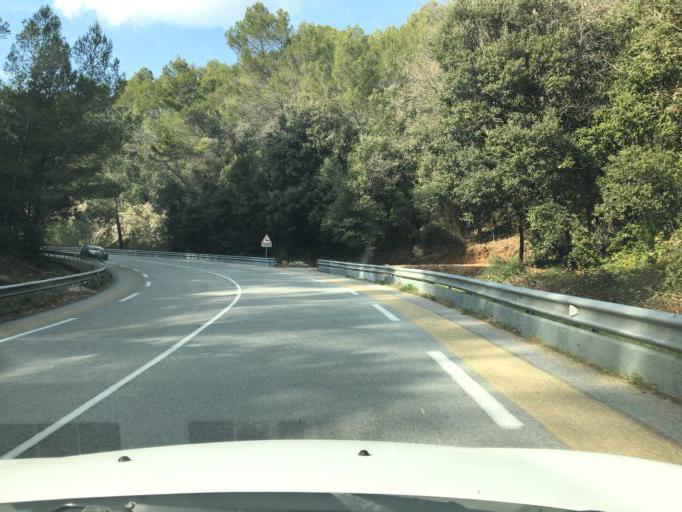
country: FR
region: Provence-Alpes-Cote d'Azur
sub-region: Departement du Var
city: Figanieres
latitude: 43.5733
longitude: 6.5049
